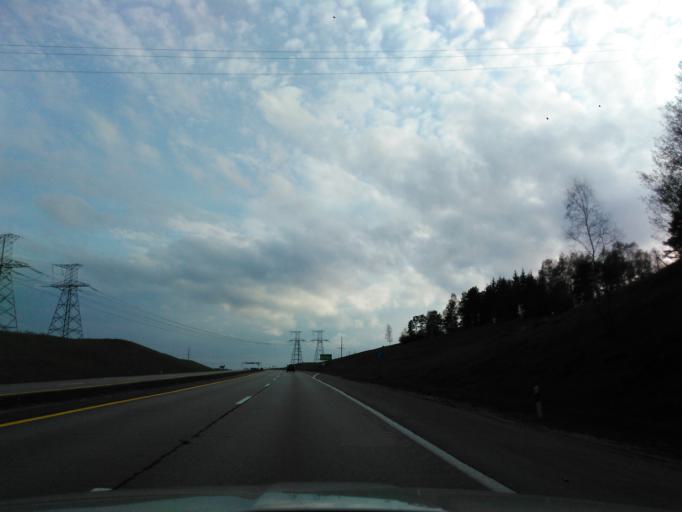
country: BY
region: Minsk
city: Astrashytski Haradok
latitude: 54.0623
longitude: 27.7109
